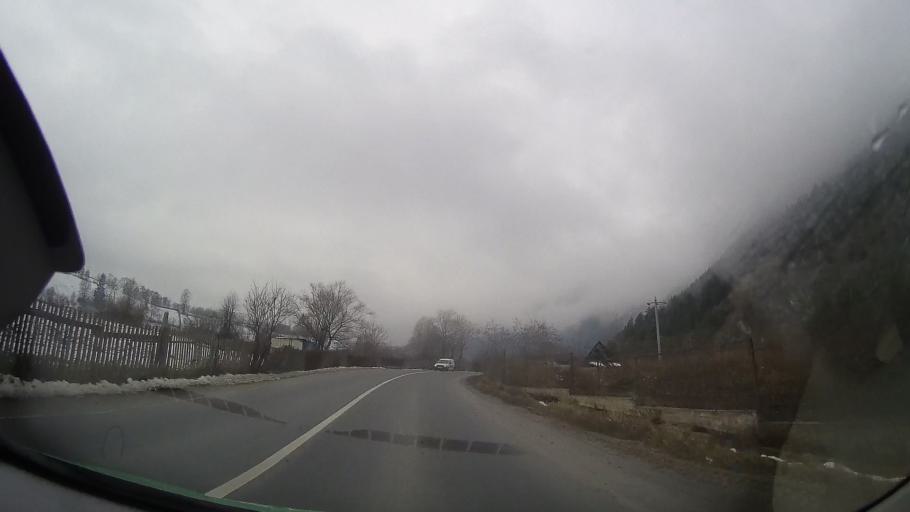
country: RO
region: Neamt
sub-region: Comuna Bicazu Ardelean
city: Bicazu Ardelean
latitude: 46.8403
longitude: 25.9066
